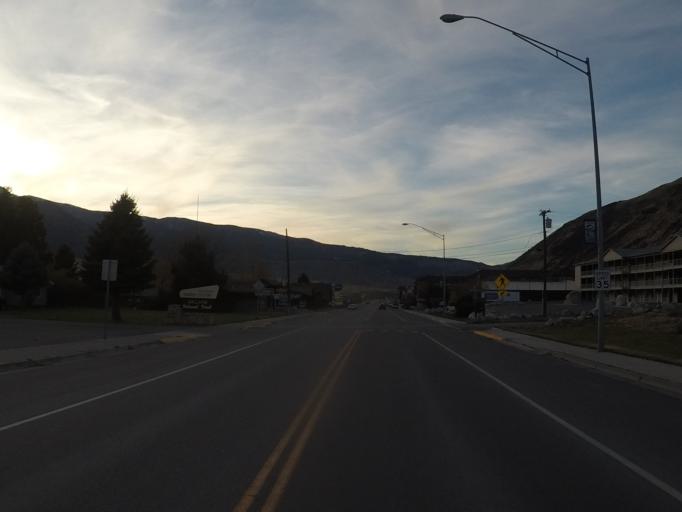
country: US
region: Montana
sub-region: Gallatin County
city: West Yellowstone
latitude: 45.0356
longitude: -110.7134
